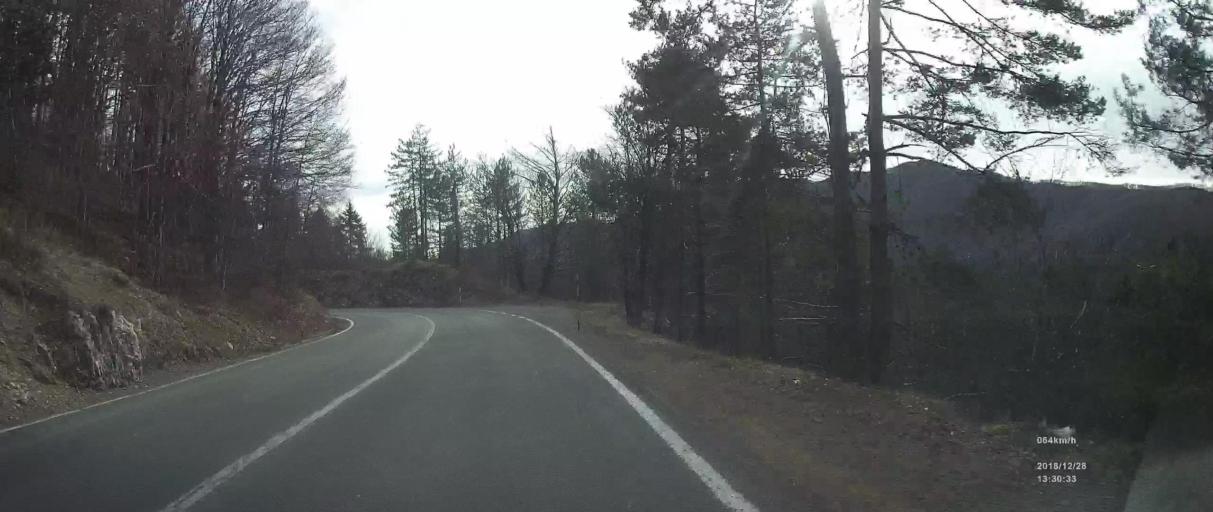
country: HR
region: Primorsko-Goranska
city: Hreljin
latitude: 45.3564
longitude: 14.6421
